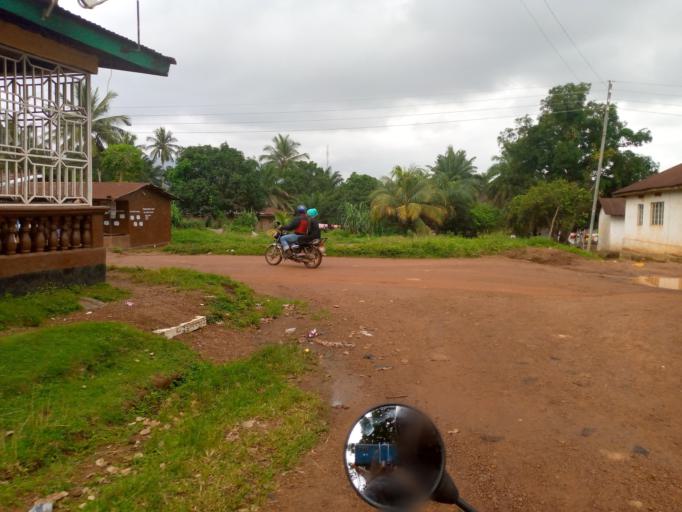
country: SL
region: Eastern Province
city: Kenema
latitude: 7.8629
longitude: -11.1934
